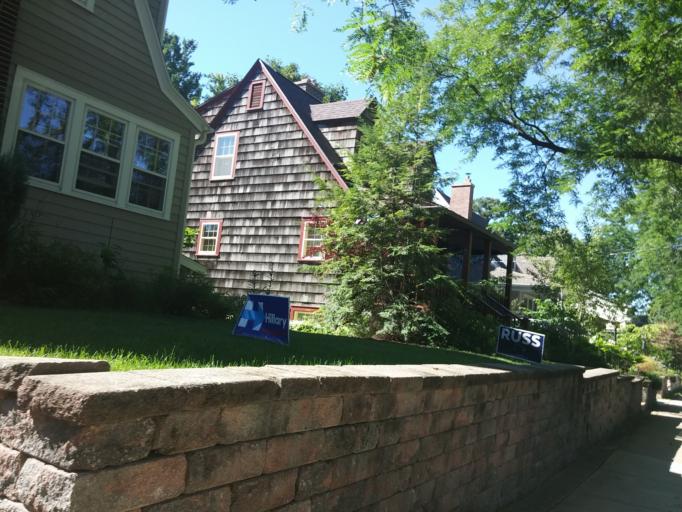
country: US
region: Wisconsin
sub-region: Dane County
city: Madison
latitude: 43.0611
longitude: -89.4246
